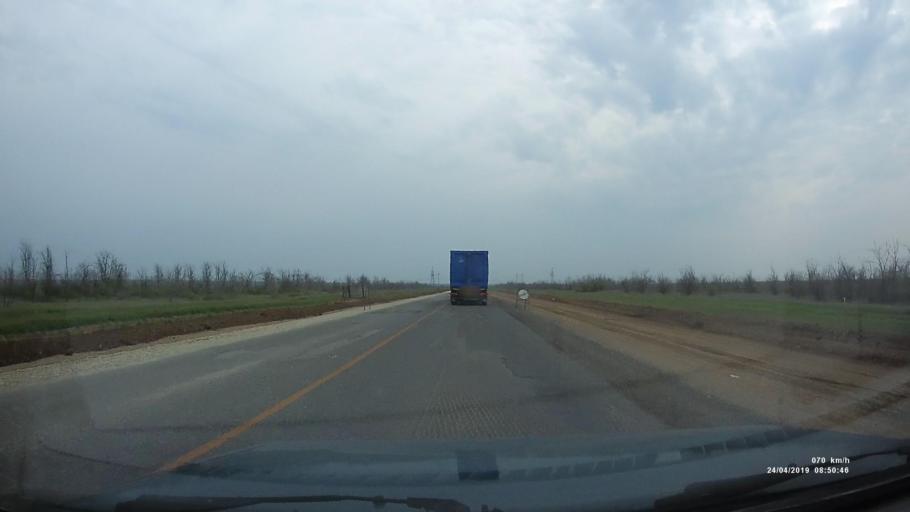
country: RU
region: Kalmykiya
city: Arshan'
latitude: 46.2635
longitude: 44.1413
